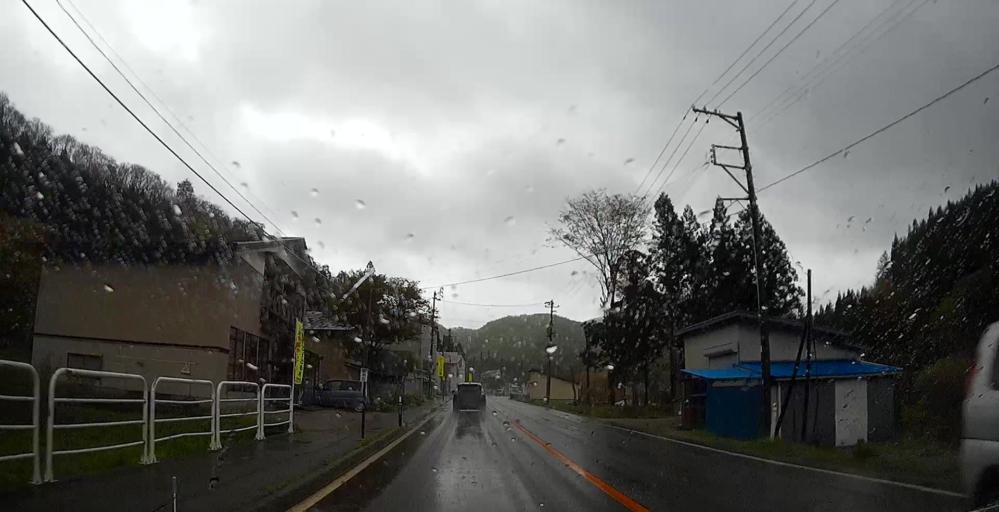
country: JP
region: Yamagata
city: Nagai
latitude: 38.0468
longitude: 139.8292
